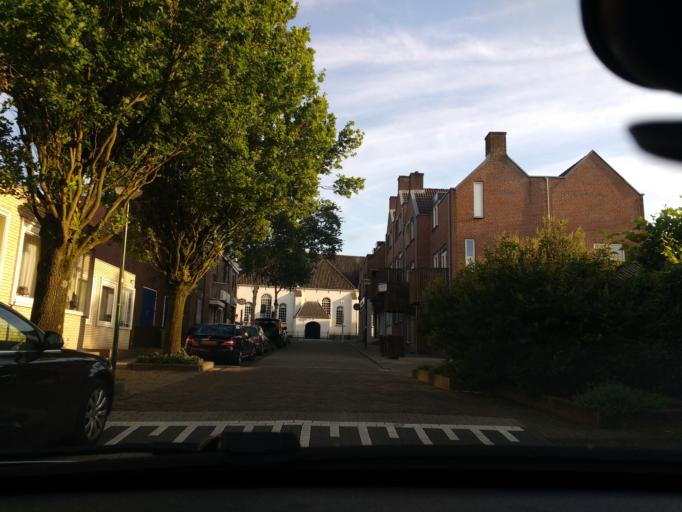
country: NL
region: Utrecht
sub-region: Gemeente Veenendaal
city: Veenendaal
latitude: 52.0268
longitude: 5.5538
